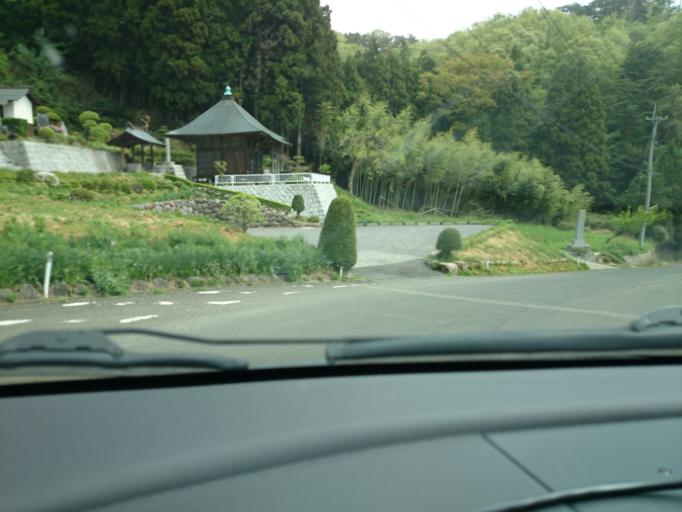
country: JP
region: Fukushima
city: Nihommatsu
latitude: 37.6054
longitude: 140.4254
